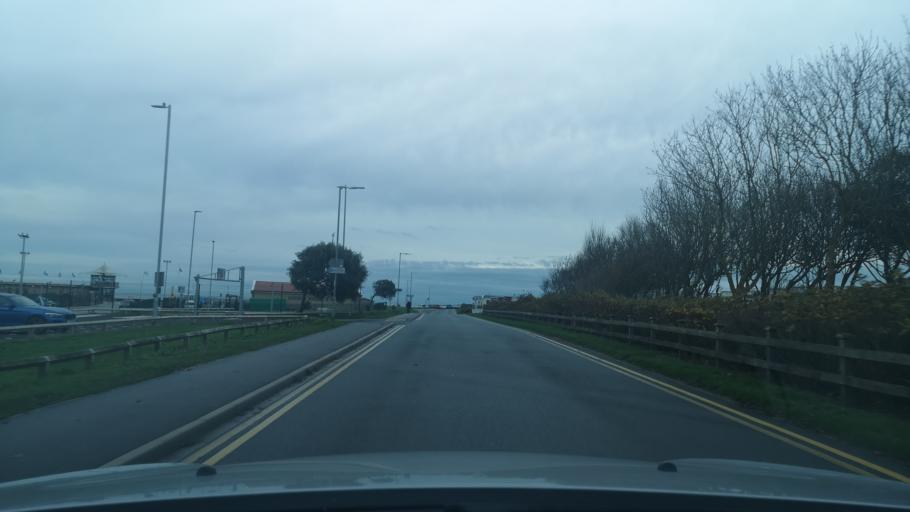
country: GB
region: England
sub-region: East Riding of Yorkshire
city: Hornsea
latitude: 53.9081
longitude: -0.1610
